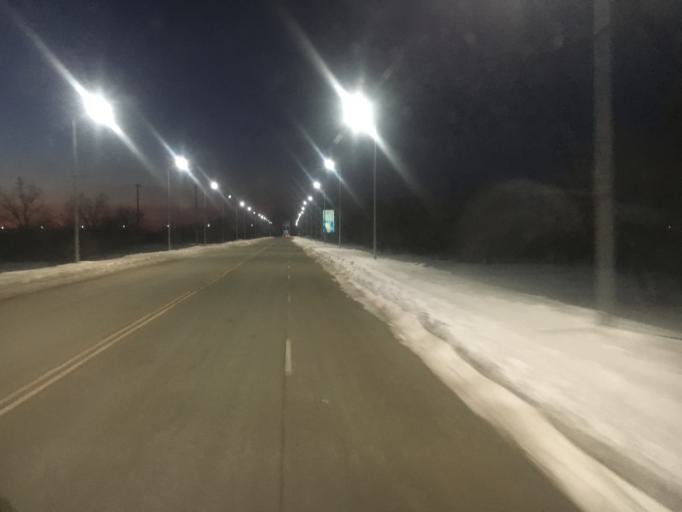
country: KZ
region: Batys Qazaqstan
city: Oral
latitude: 51.1619
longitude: 51.5282
